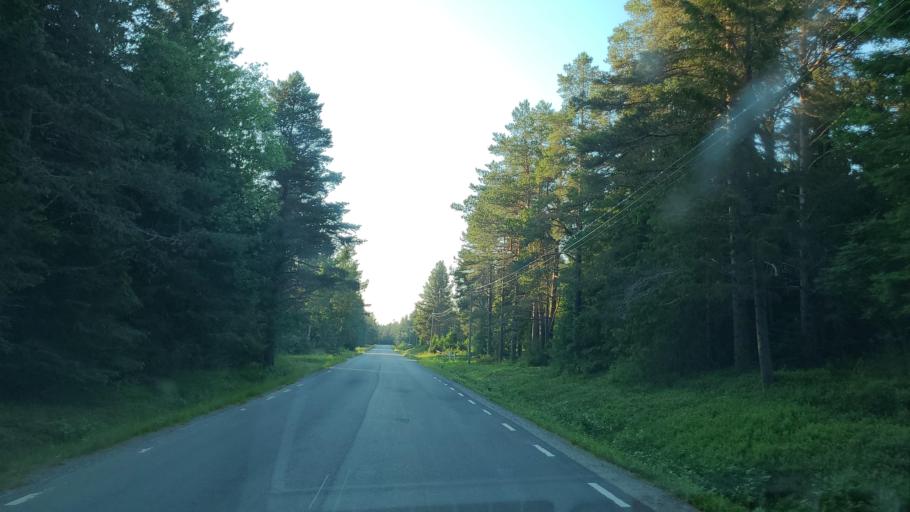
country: SE
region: Vaesterbotten
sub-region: Skelleftea Kommun
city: Skelleftehamn
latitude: 64.4680
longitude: 21.5857
